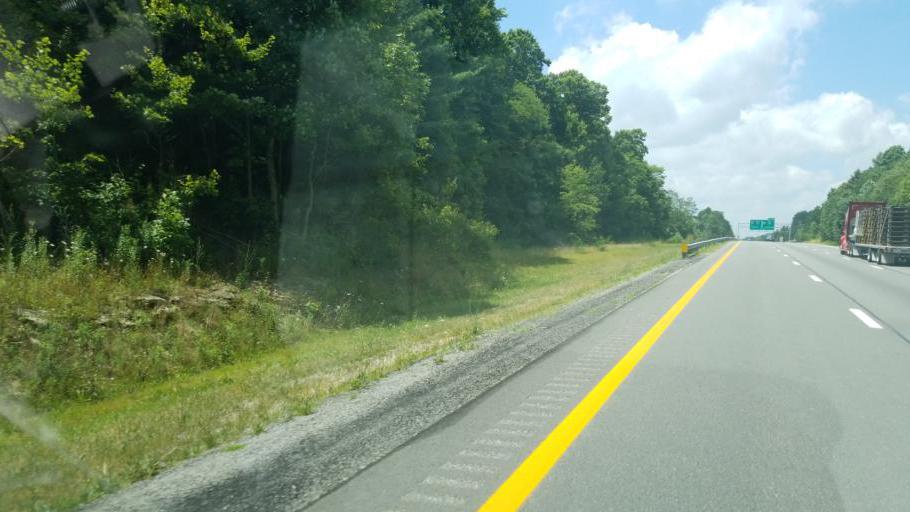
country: US
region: West Virginia
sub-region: Raleigh County
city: MacArthur
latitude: 37.7245
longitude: -81.1838
